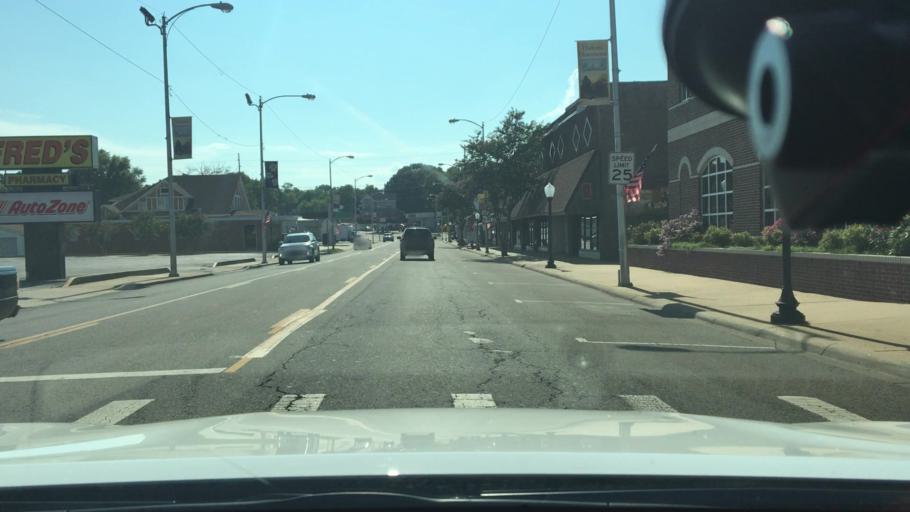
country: US
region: Arkansas
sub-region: Johnson County
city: Clarksville
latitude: 35.4712
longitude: -93.4665
